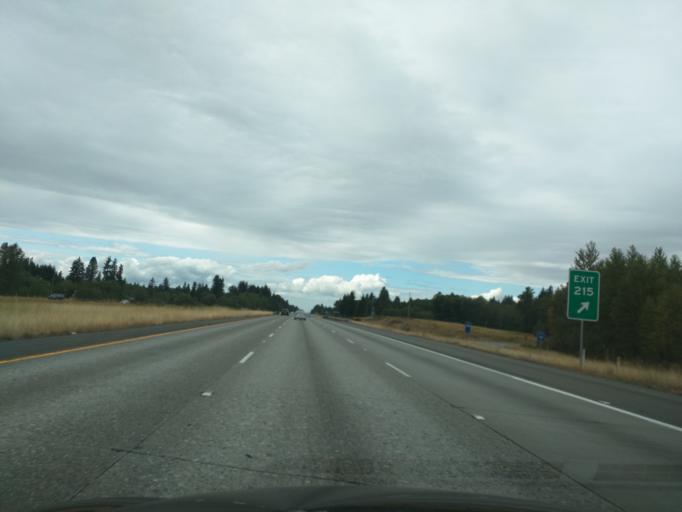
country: US
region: Washington
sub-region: Snohomish County
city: Stanwood
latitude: 48.2663
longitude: -122.2669
